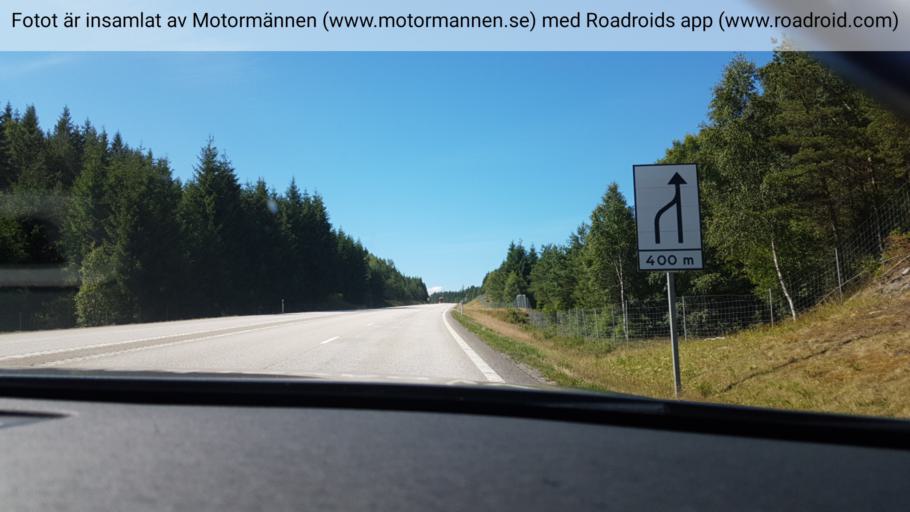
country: SE
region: Vaestra Goetaland
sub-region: Marks Kommun
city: Fritsla
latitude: 57.5643
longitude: 12.8335
